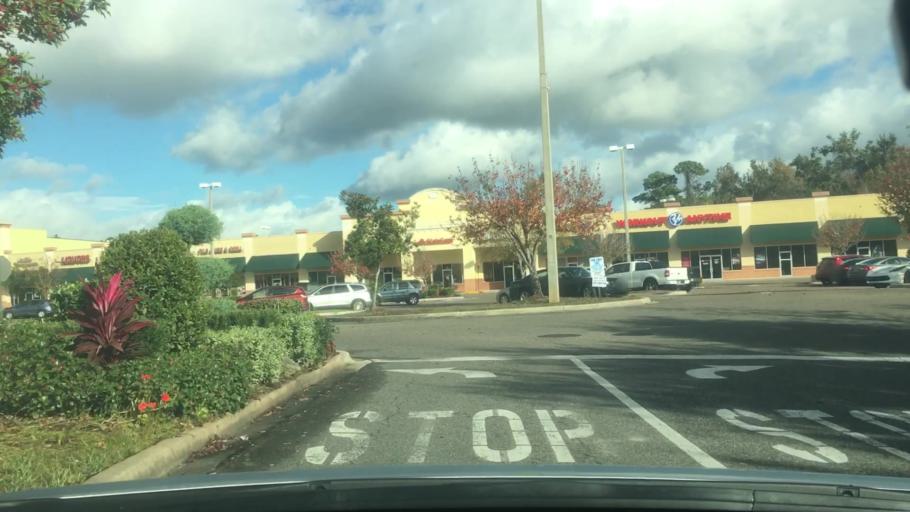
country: US
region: Florida
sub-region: Nassau County
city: Yulee
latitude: 30.4843
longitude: -81.6041
